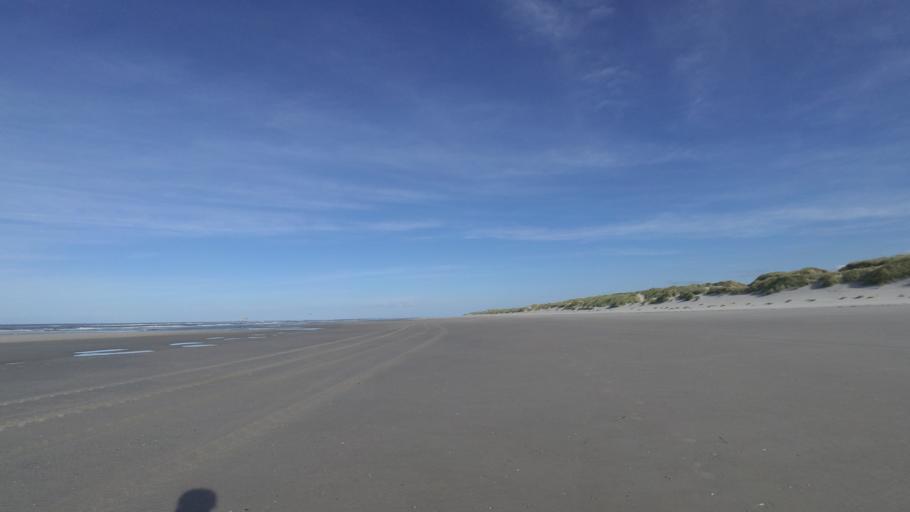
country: NL
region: Friesland
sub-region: Gemeente Ameland
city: Nes
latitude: 53.4658
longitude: 5.8665
